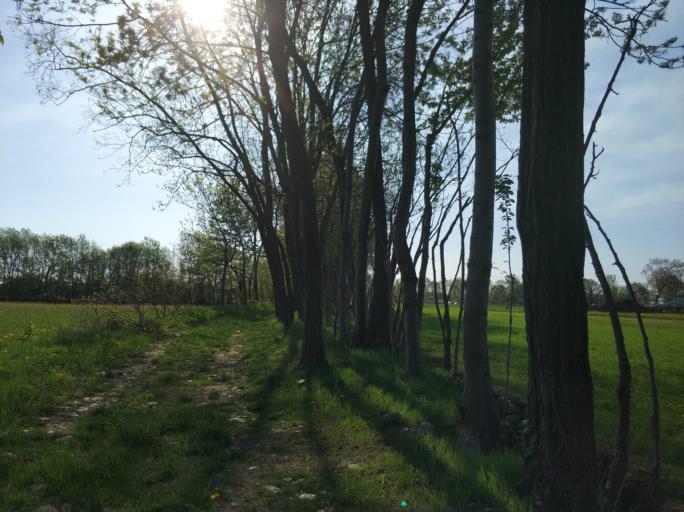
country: IT
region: Piedmont
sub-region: Provincia di Torino
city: Nole
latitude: 45.2322
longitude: 7.5829
